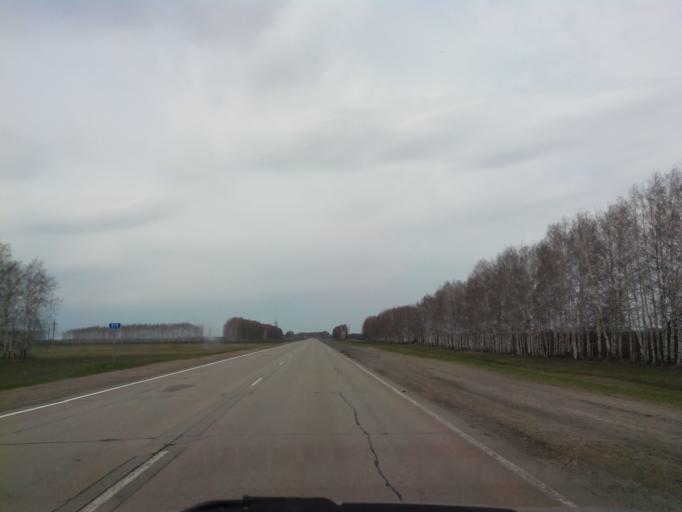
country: RU
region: Tambov
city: Satinka
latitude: 52.2334
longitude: 41.5382
